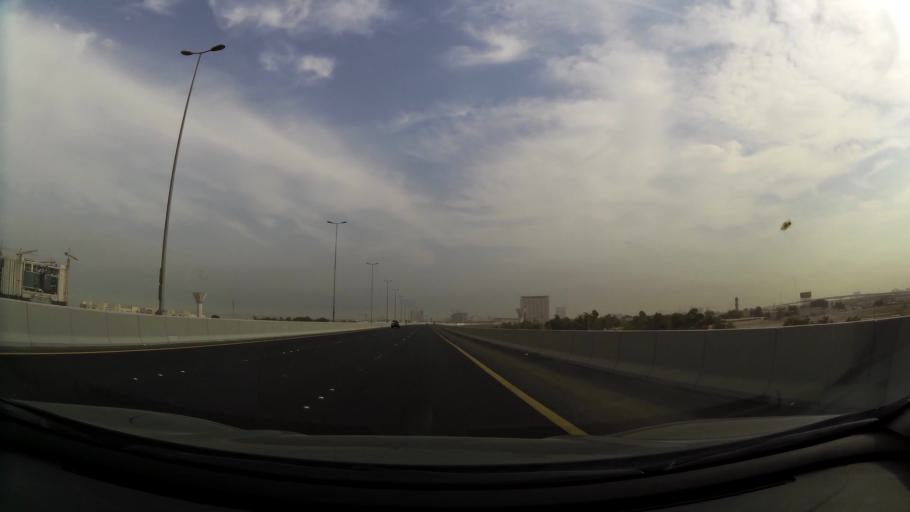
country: KW
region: Al Asimah
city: Ar Rabiyah
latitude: 29.3198
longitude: 47.8848
